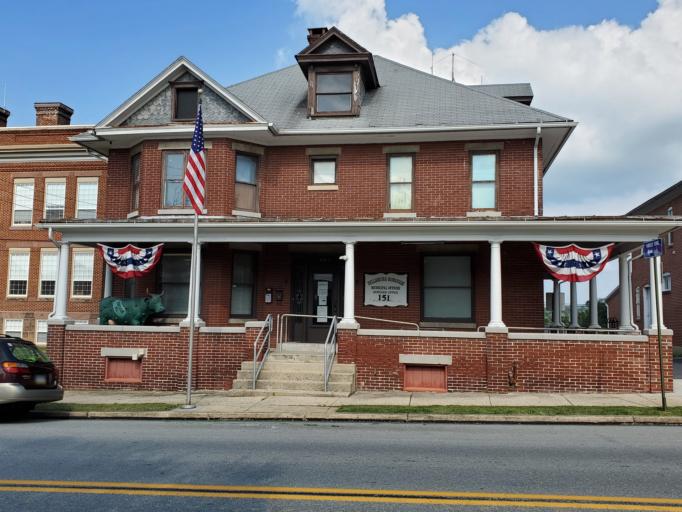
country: US
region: Pennsylvania
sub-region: York County
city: Dillsburg
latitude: 40.1078
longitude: -77.0350
